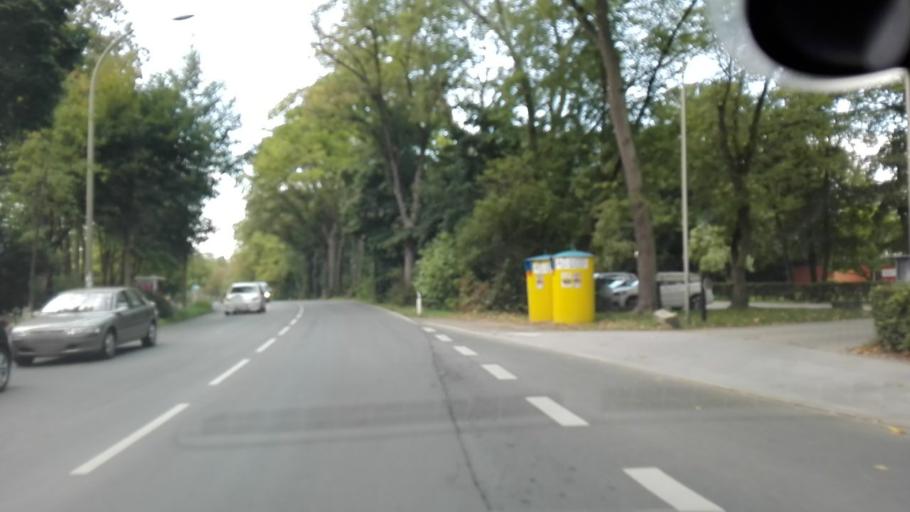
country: DE
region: North Rhine-Westphalia
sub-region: Regierungsbezirk Arnsberg
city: Dortmund
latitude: 51.4827
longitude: 7.4282
